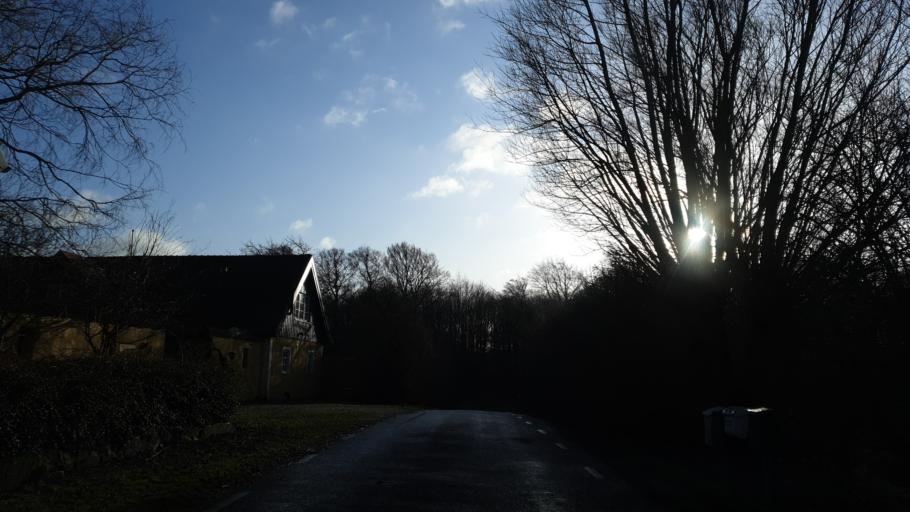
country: SE
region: Skane
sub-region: Svedala Kommun
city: Svedala
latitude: 55.4976
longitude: 13.2890
